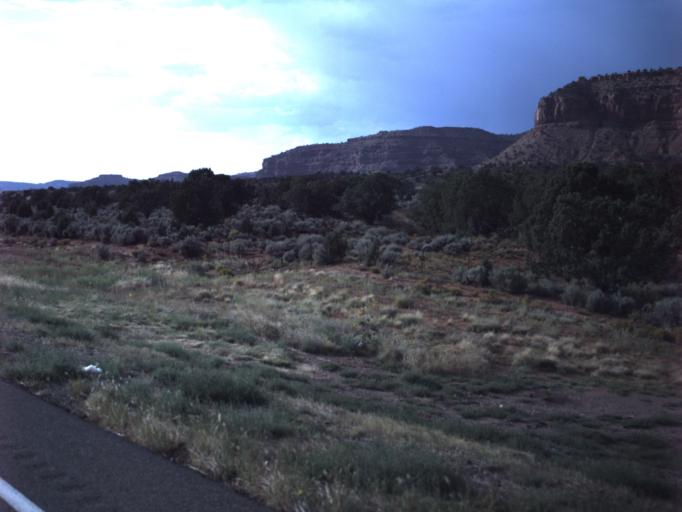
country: US
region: Utah
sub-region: Kane County
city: Kanab
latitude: 37.0278
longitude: -112.4780
